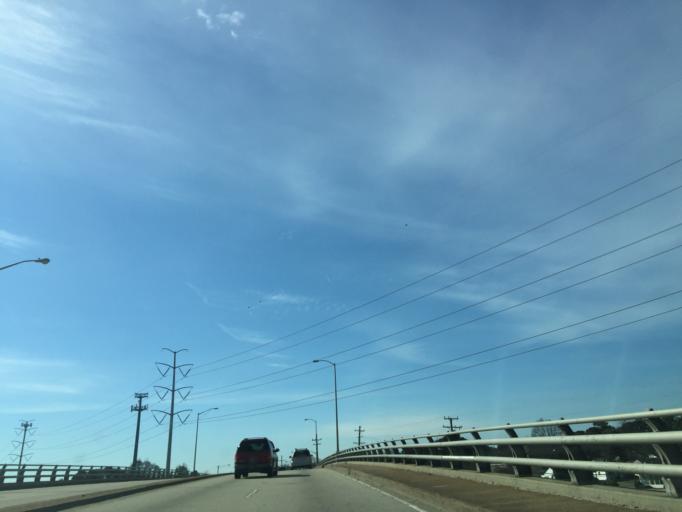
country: US
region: Virginia
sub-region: City of Norfolk
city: Norfolk
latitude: 36.8978
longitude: -76.2560
